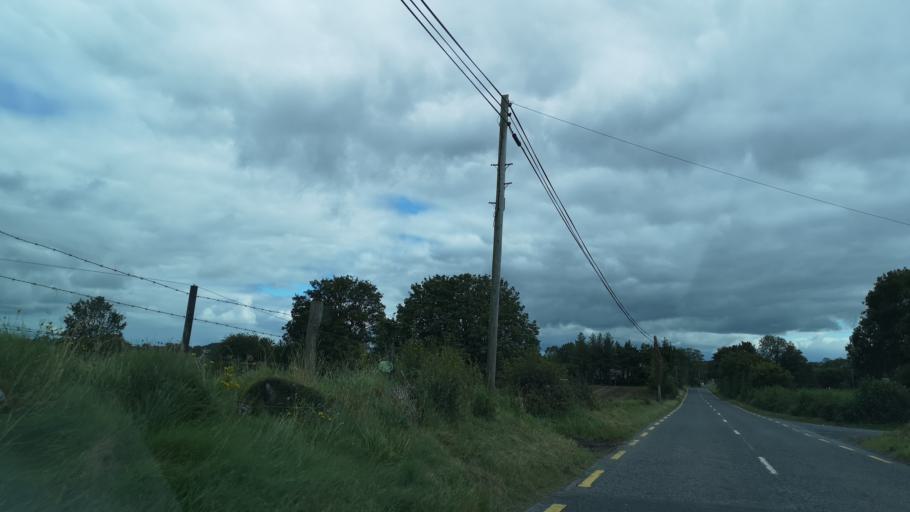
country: IE
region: Connaught
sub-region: County Galway
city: Ballinasloe
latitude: 53.3034
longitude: -8.1356
